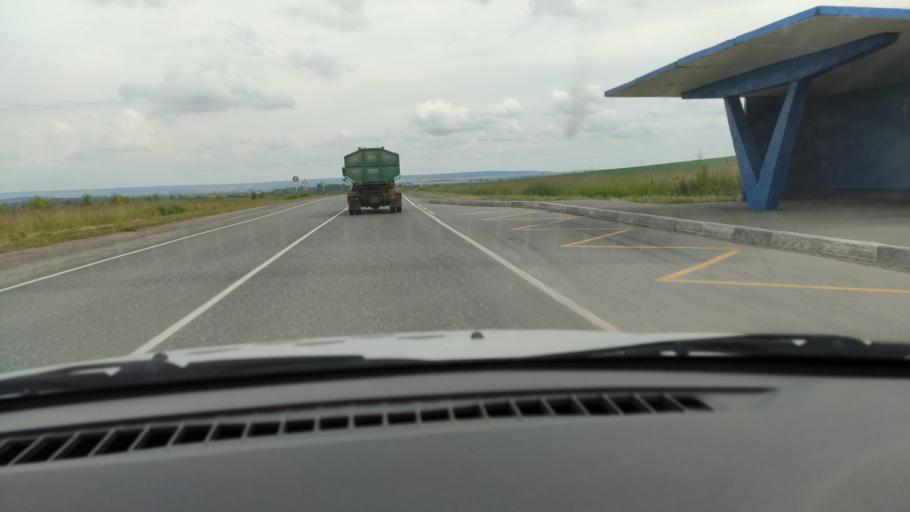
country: RU
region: Perm
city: Froly
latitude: 57.9033
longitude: 56.2068
